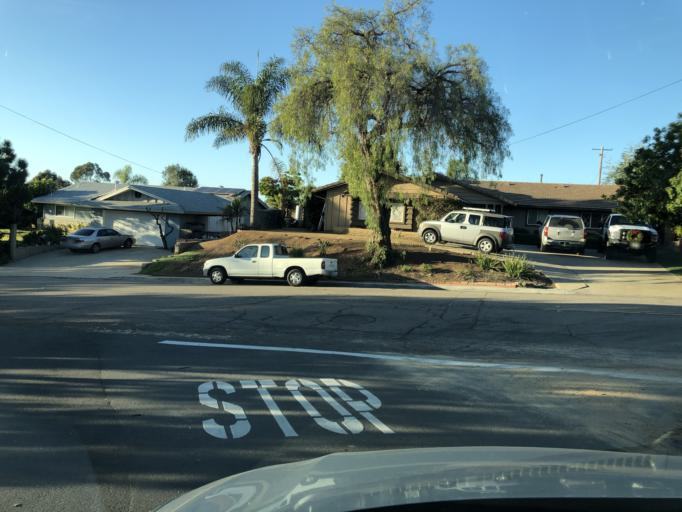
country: US
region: California
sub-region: San Diego County
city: Chula Vista
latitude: 32.6537
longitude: -117.0622
